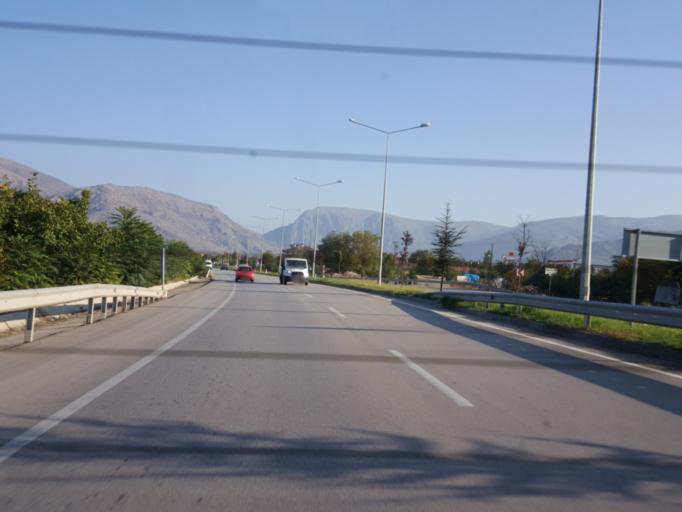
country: TR
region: Amasya
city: Amasya
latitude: 40.5903
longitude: 35.8018
